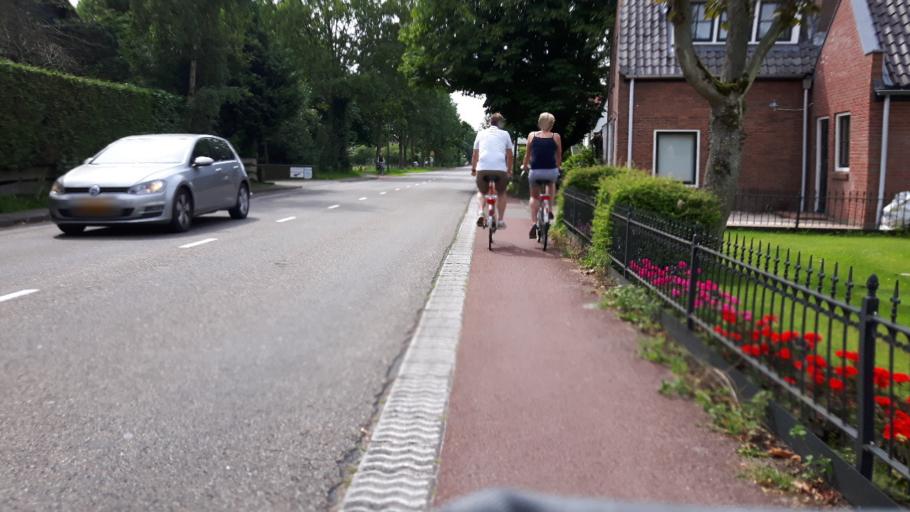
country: NL
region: North Holland
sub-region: Gemeente Wijdemeren
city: Oud-Loosdrecht
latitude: 52.2070
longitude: 5.1057
